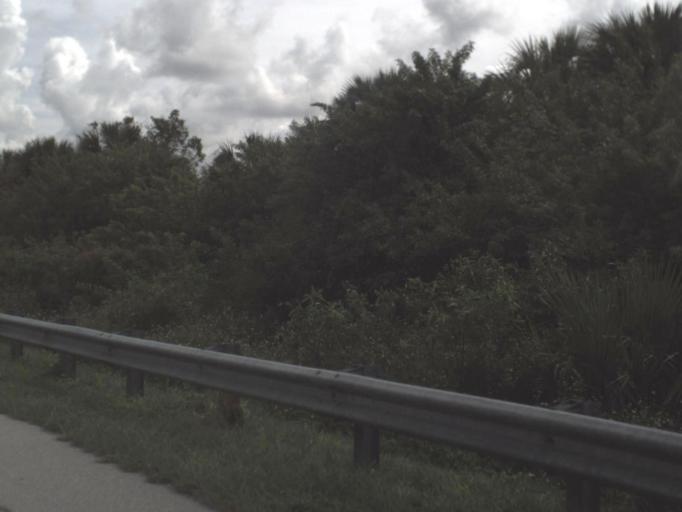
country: US
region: Florida
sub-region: Glades County
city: Buckhead Ridge
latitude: 27.2309
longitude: -81.0866
